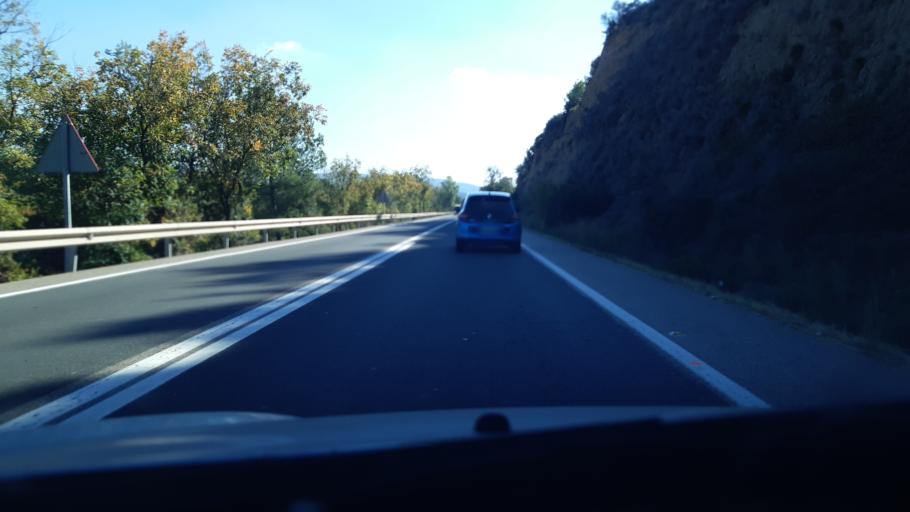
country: ES
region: Catalonia
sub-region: Provincia de Tarragona
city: Tivenys
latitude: 40.8609
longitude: 0.5091
